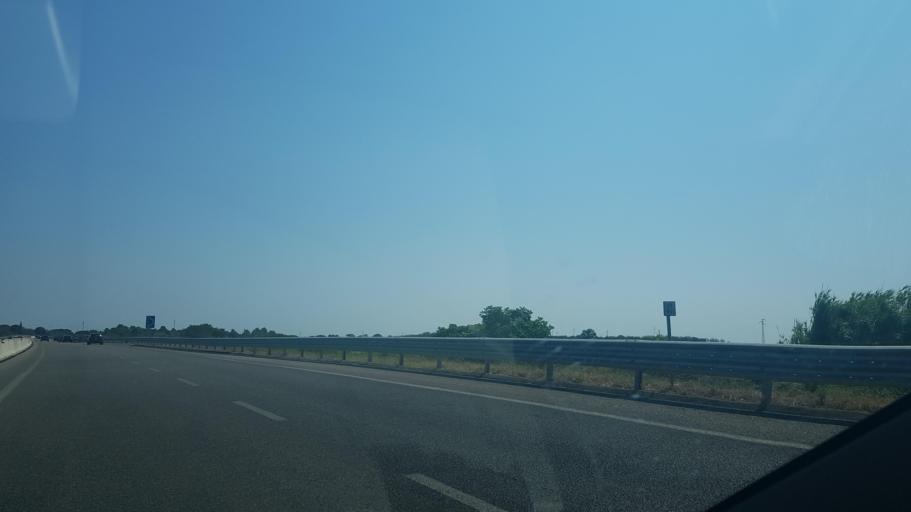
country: IT
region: Apulia
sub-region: Provincia di Lecce
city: Palmariggi
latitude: 40.1279
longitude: 18.3855
